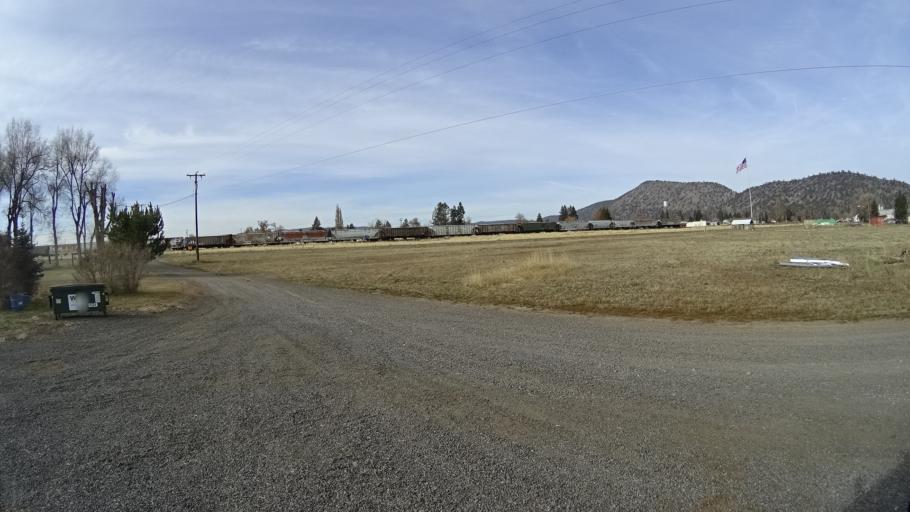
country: US
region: Oregon
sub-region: Klamath County
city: Klamath Falls
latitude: 41.9598
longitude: -121.9178
